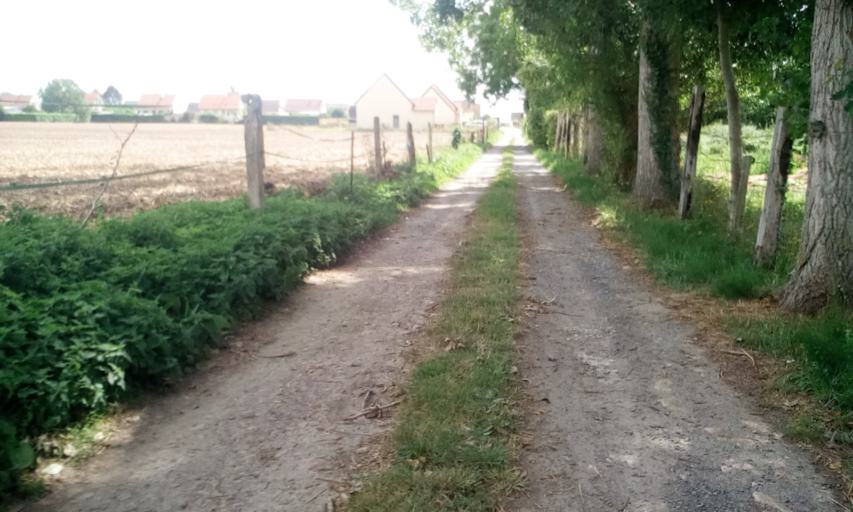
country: FR
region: Lower Normandy
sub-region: Departement du Calvados
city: Bellengreville
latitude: 49.1106
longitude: -0.2104
